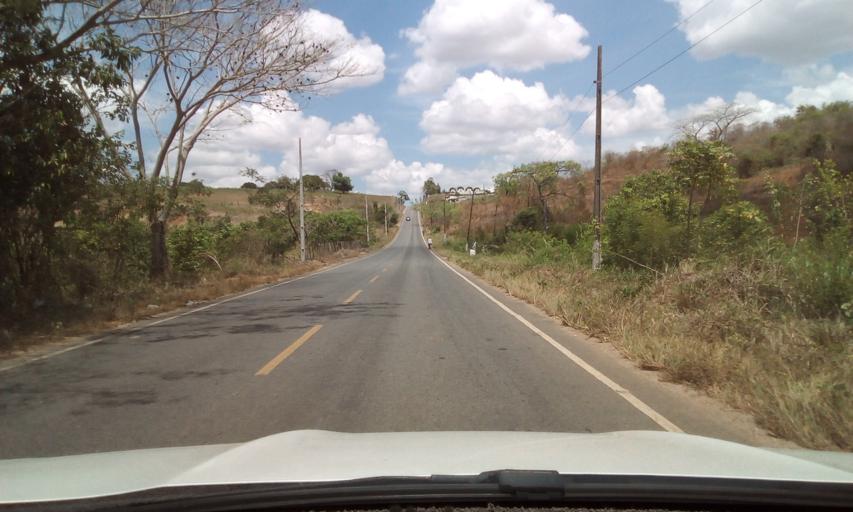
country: BR
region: Paraiba
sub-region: Guarabira
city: Guarabira
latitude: -6.8785
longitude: -35.5013
